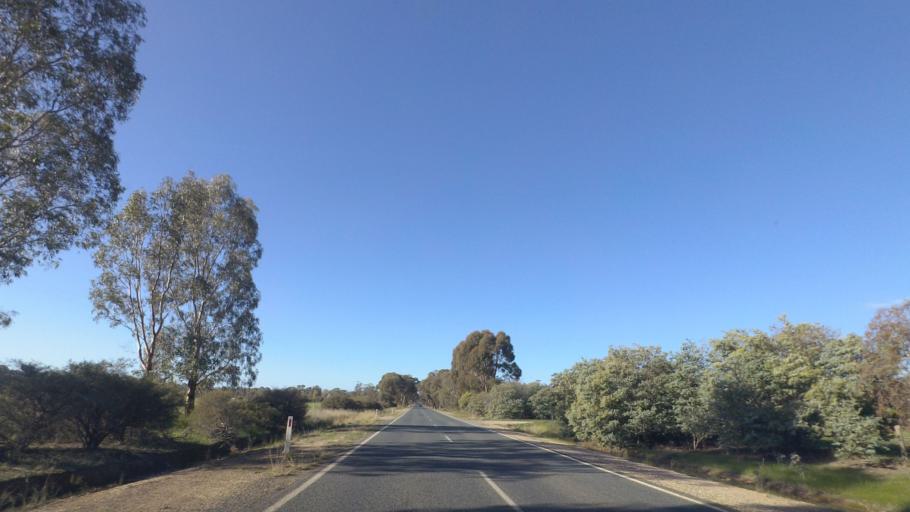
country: AU
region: Victoria
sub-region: Greater Bendigo
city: Epsom
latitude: -36.6749
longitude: 144.3972
